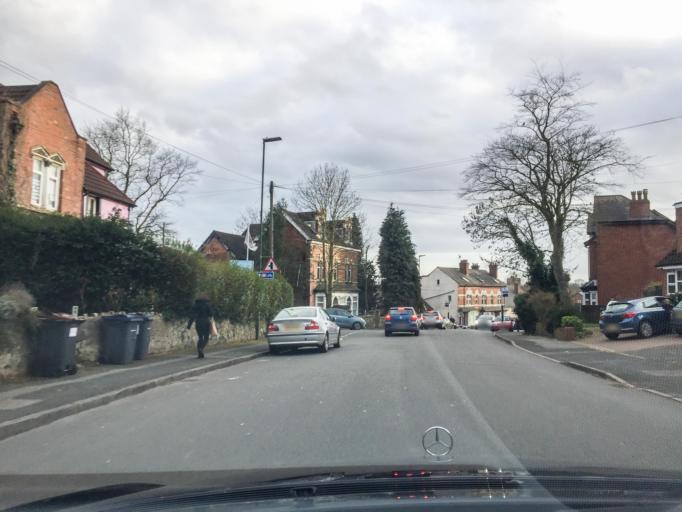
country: GB
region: England
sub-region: City and Borough of Birmingham
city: Bartley Green
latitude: 52.4114
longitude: -1.9608
